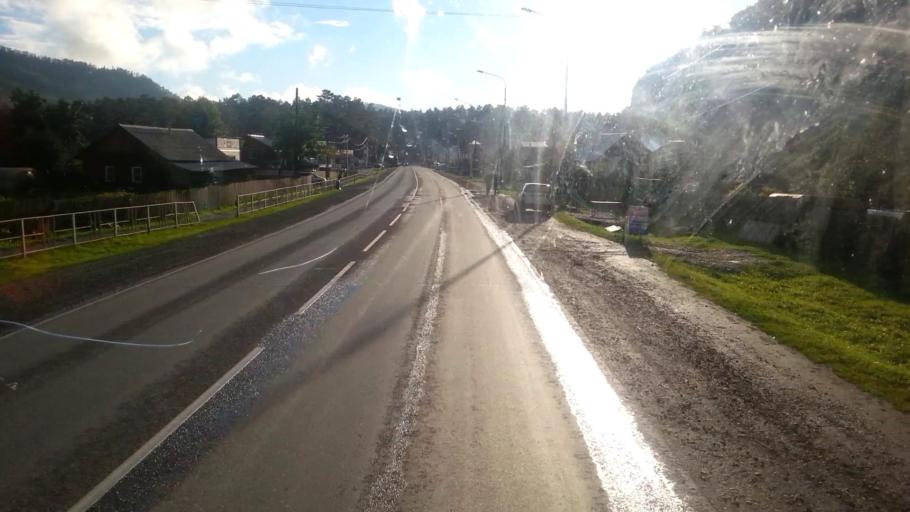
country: RU
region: Altay
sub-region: Mayminskiy Rayon
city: Manzherok
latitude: 51.8337
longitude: 85.7731
